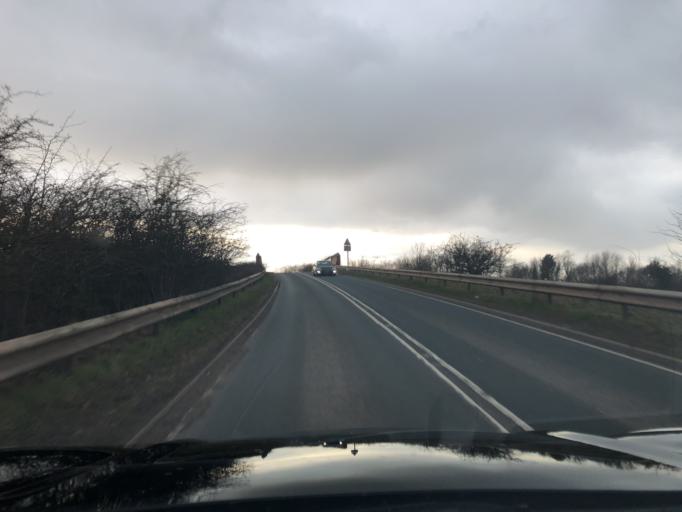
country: GB
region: England
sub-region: North Yorkshire
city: Northallerton
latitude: 54.3456
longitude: -1.4474
